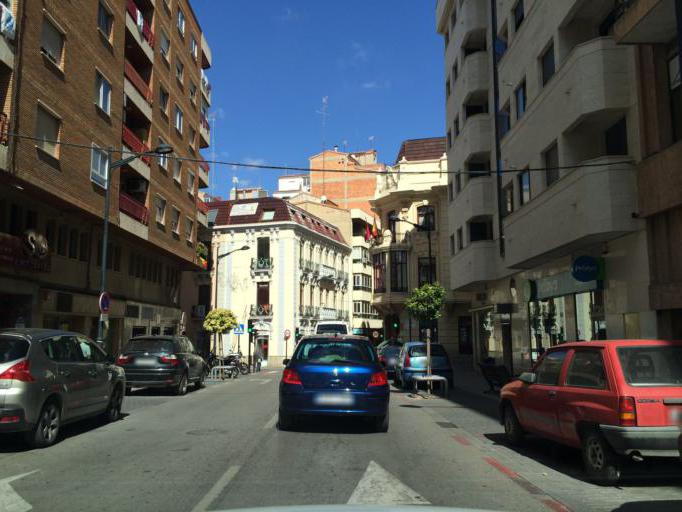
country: ES
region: Castille-La Mancha
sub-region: Provincia de Albacete
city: Albacete
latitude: 38.9956
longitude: -1.8569
